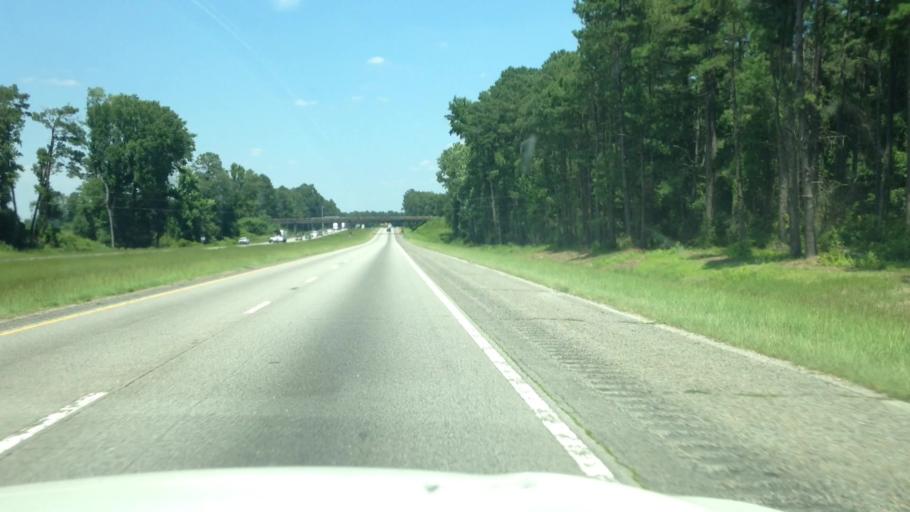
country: US
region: North Carolina
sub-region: Robeson County
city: Rowland
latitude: 34.4834
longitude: -79.3359
